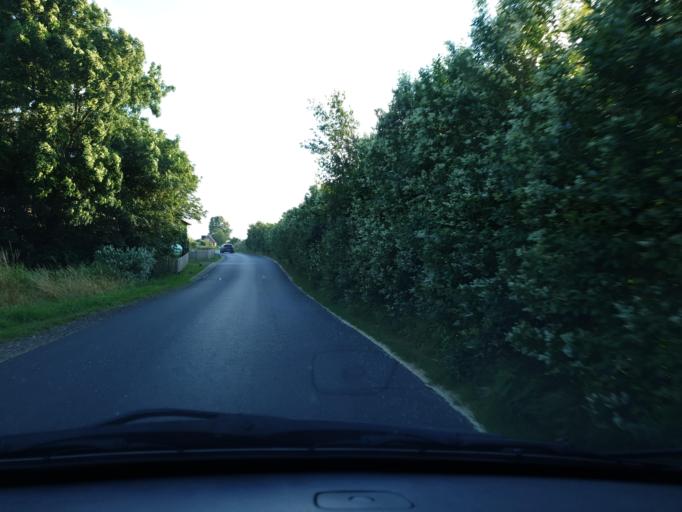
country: DE
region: Schleswig-Holstein
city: Elpersbuttel
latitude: 54.0749
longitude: 9.0206
